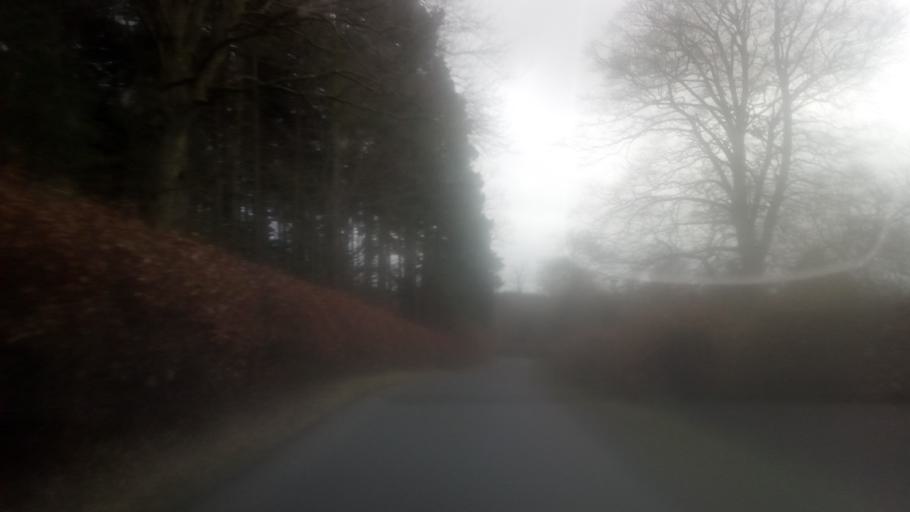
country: GB
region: Scotland
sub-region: The Scottish Borders
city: Jedburgh
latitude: 55.4803
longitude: -2.5254
